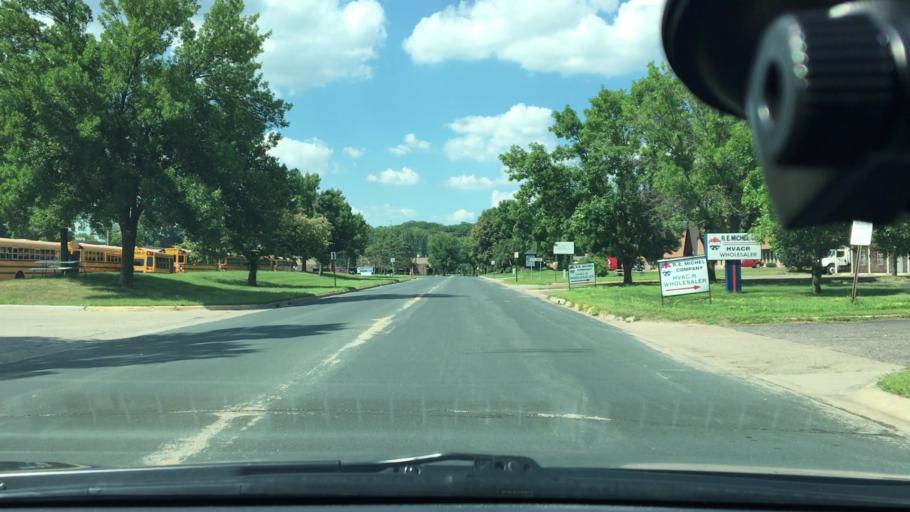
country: US
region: Minnesota
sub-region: Hennepin County
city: Golden Valley
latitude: 44.9865
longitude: -93.3929
